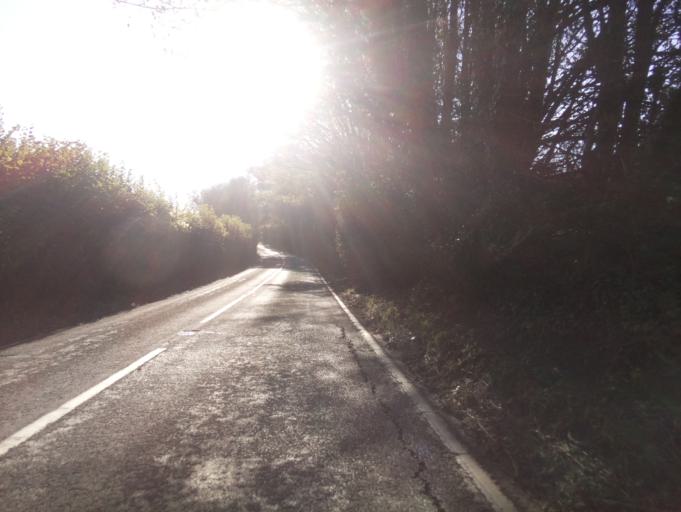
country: GB
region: England
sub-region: Dorset
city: Sherborne
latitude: 50.8448
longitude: -2.4616
